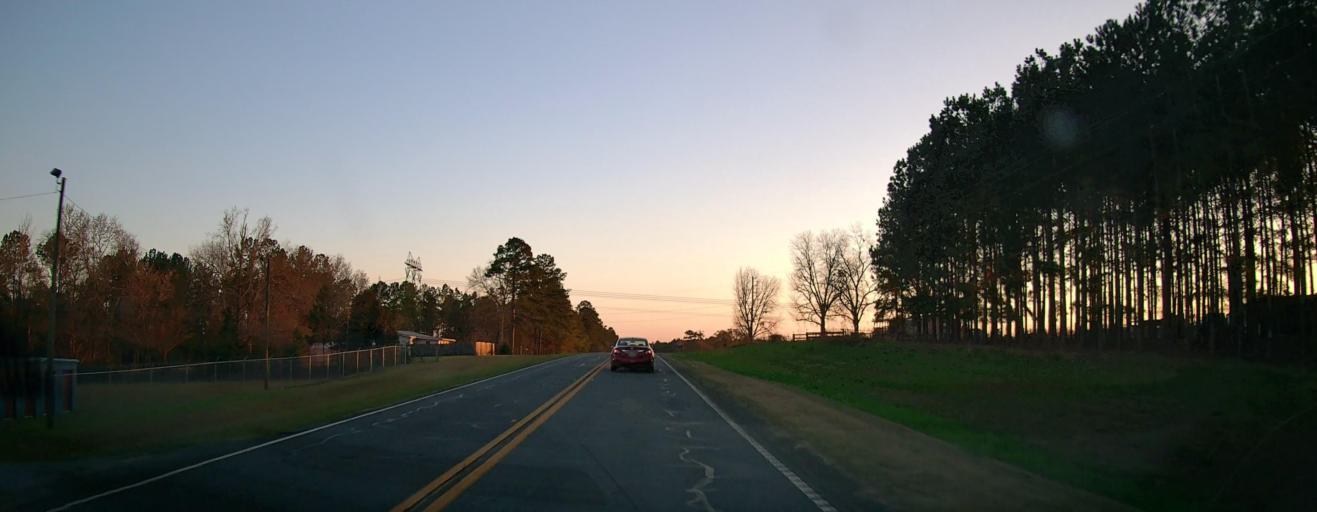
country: US
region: Georgia
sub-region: Dodge County
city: Eastman
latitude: 32.2509
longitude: -83.1420
